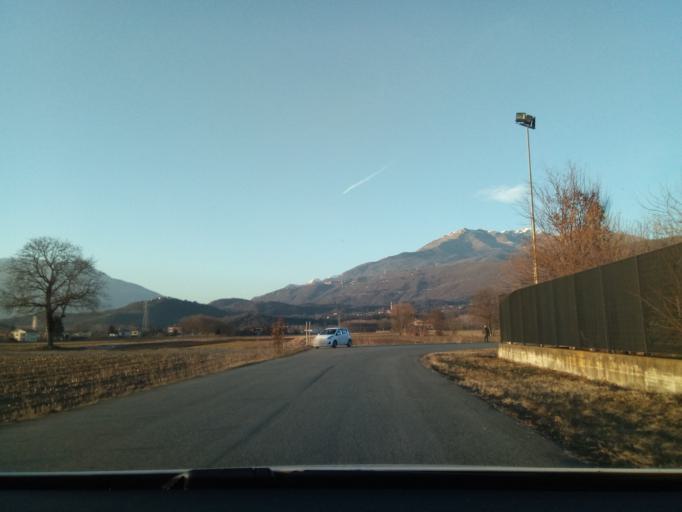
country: IT
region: Piedmont
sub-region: Provincia di Torino
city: Cascinette d'Ivrea
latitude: 45.4744
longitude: 7.9163
